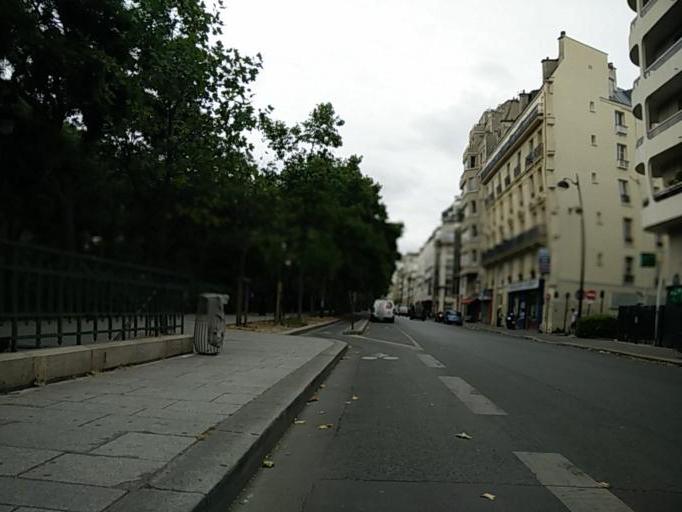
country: FR
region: Ile-de-France
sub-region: Paris
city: Paris
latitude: 48.8594
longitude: 2.3717
